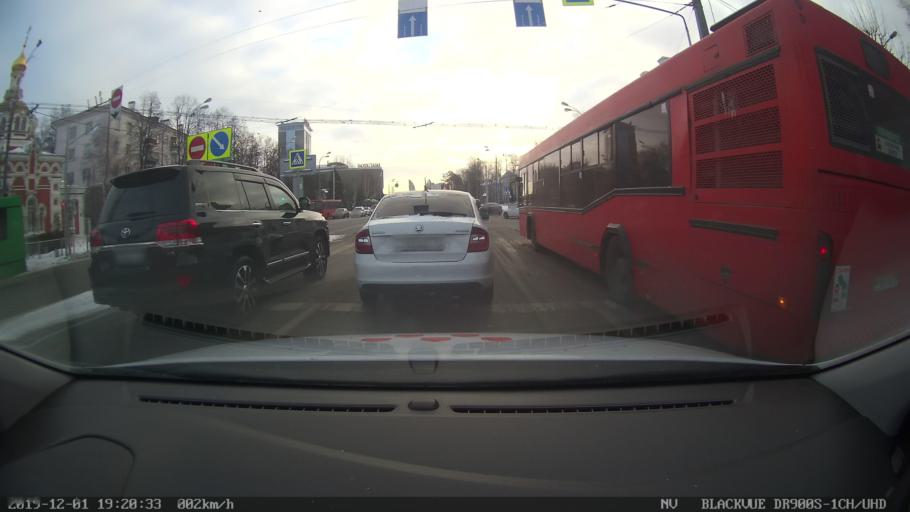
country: RU
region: Tatarstan
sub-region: Gorod Kazan'
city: Kazan
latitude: 55.8002
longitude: 49.1433
